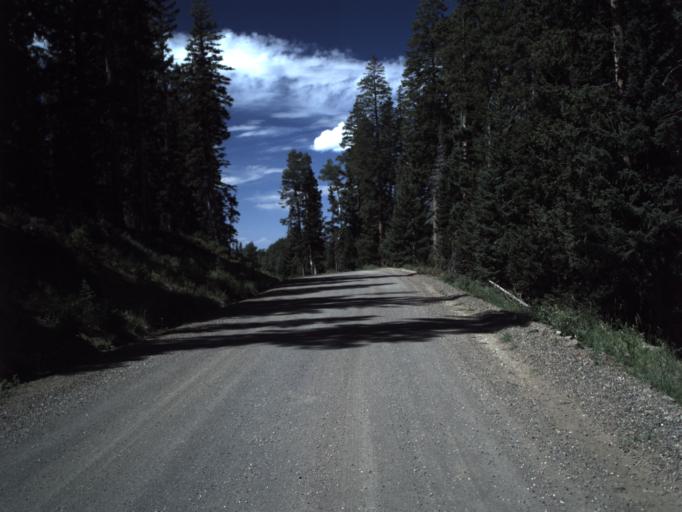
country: US
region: Utah
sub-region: Piute County
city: Junction
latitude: 38.2619
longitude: -112.3755
